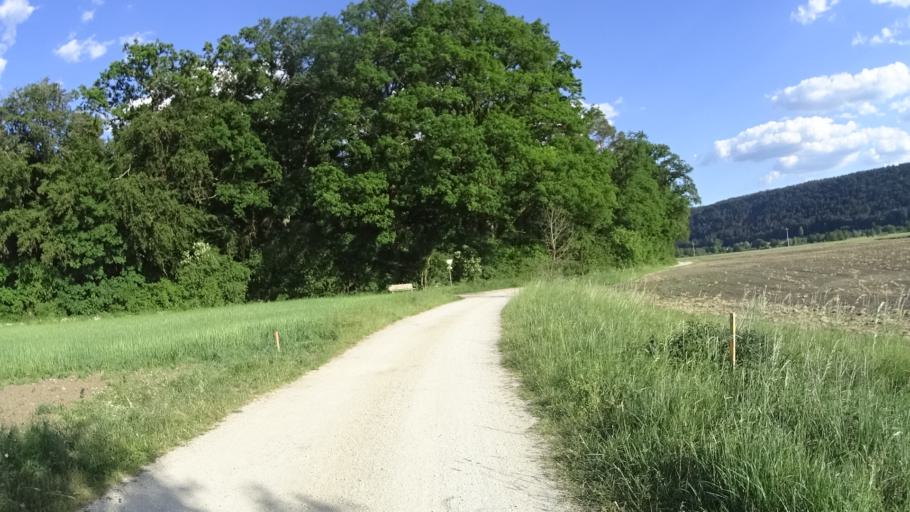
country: DE
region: Bavaria
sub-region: Upper Palatinate
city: Dietfurt
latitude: 49.0268
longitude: 11.5980
